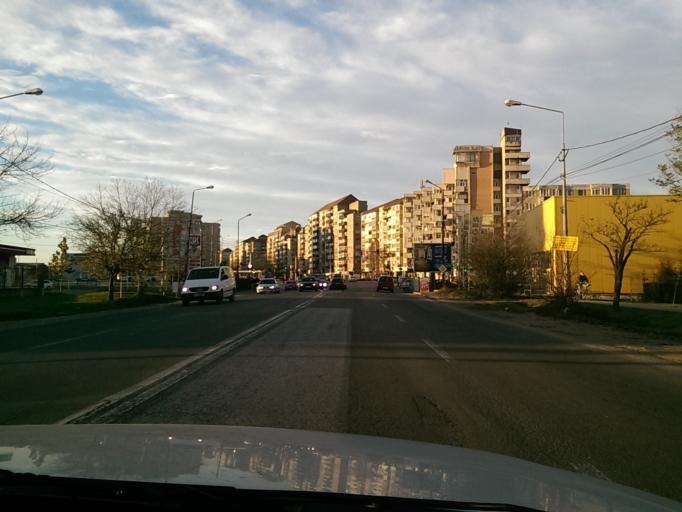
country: RO
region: Bihor
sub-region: Comuna Sanmartin
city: Sanmartin
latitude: 47.0281
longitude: 21.9568
